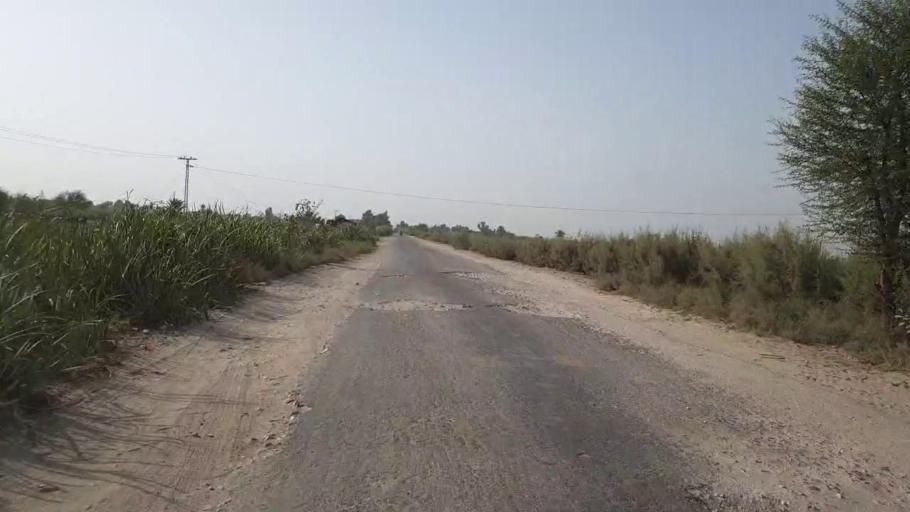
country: PK
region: Sindh
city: Khadro
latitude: 26.3297
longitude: 68.9301
